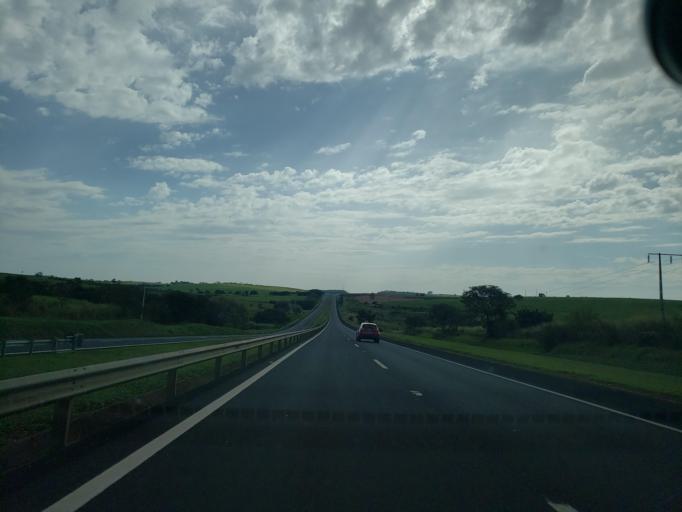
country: BR
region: Sao Paulo
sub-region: Lins
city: Lins
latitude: -21.7453
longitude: -49.6929
